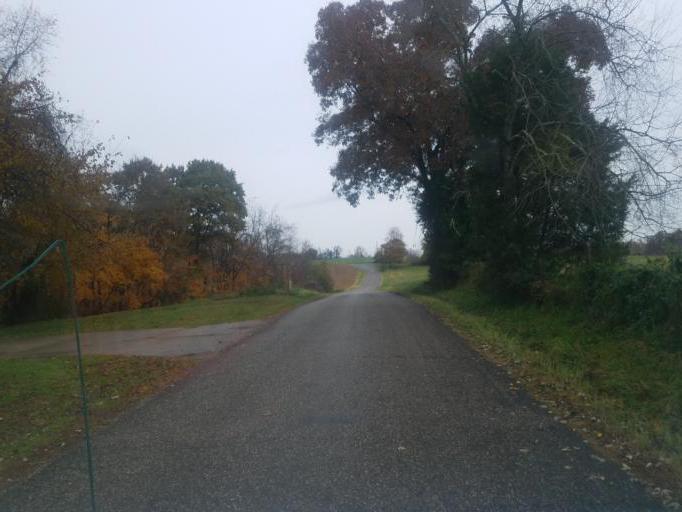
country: US
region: Ohio
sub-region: Washington County
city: Beverly
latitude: 39.5491
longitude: -81.7035
